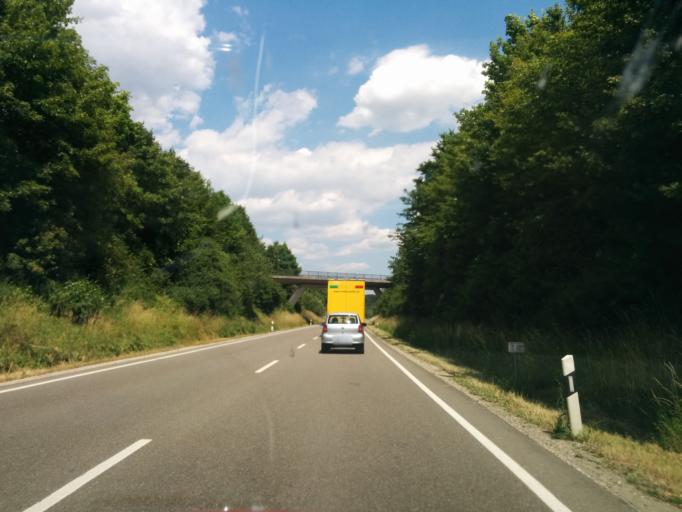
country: DE
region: Bavaria
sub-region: Swabia
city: Monheim
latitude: 48.8479
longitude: 10.8386
